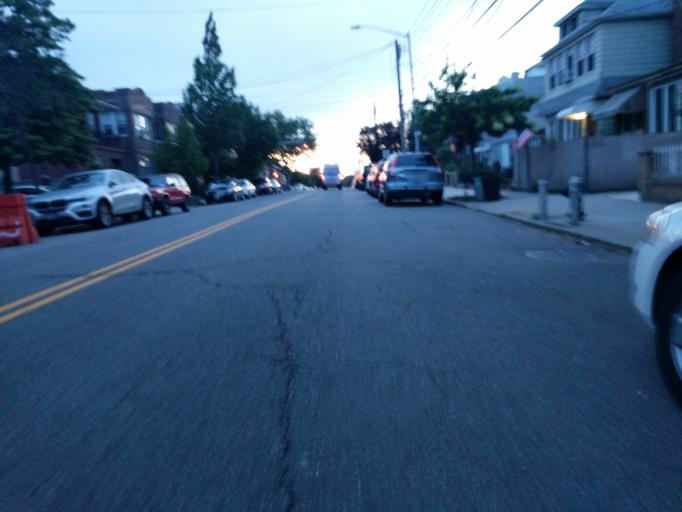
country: US
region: New York
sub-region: Queens County
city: Long Island City
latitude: 40.7728
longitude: -73.9010
